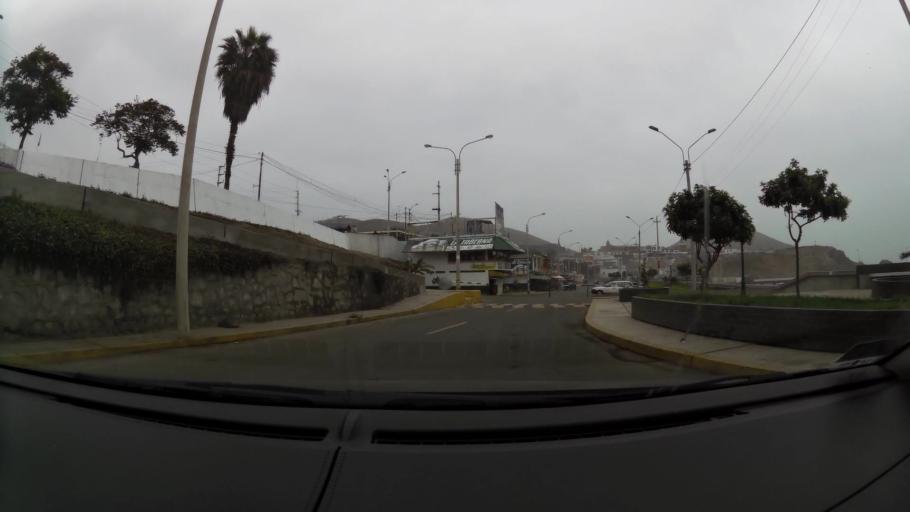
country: PE
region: Lima
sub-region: Provincia de Huaral
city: Chancay
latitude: -11.5850
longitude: -77.2715
